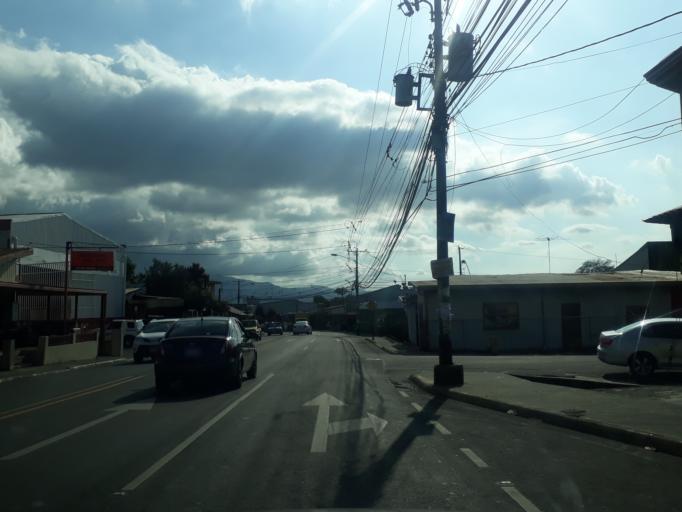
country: CR
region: San Jose
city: San Vicente
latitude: 9.9647
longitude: -84.0402
